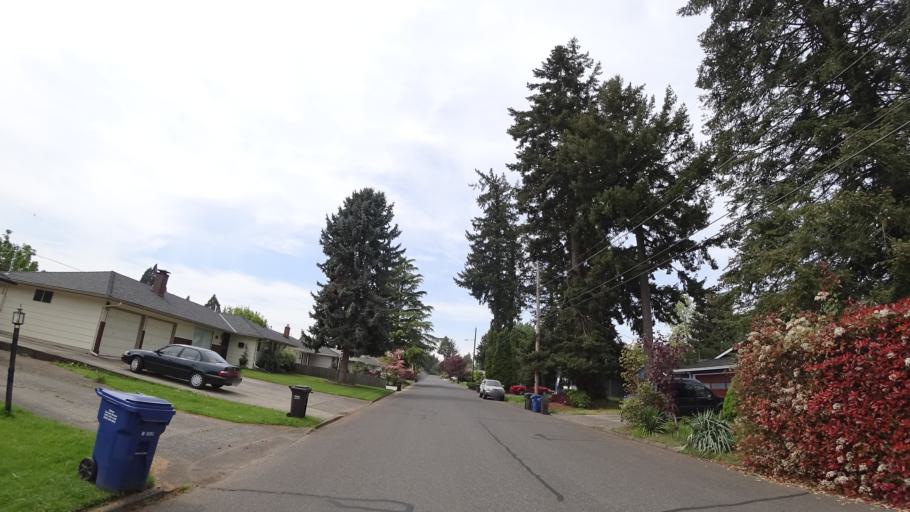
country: US
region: Oregon
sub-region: Clackamas County
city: Milwaukie
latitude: 45.4562
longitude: -122.6161
